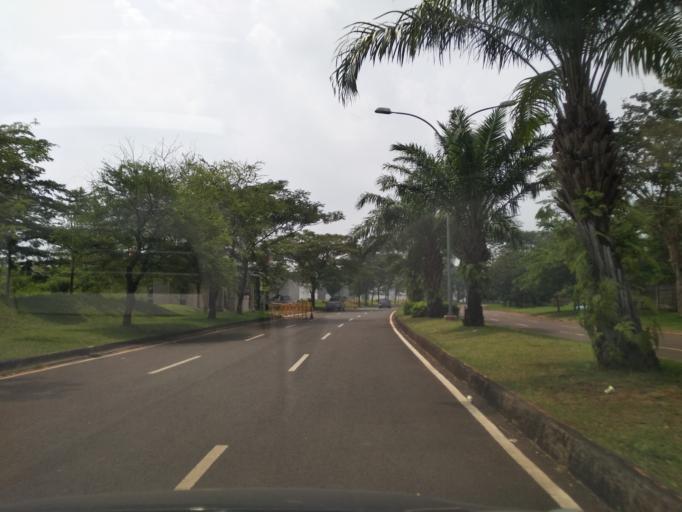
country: ID
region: West Java
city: Bekasi
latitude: -6.2941
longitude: 107.0470
